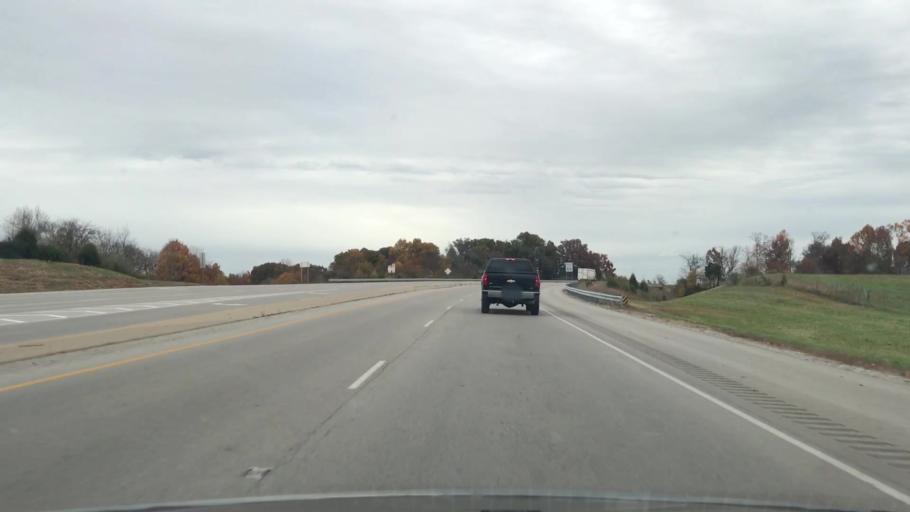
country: US
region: Kentucky
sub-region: Barren County
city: Glasgow
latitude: 37.0127
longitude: -85.9524
